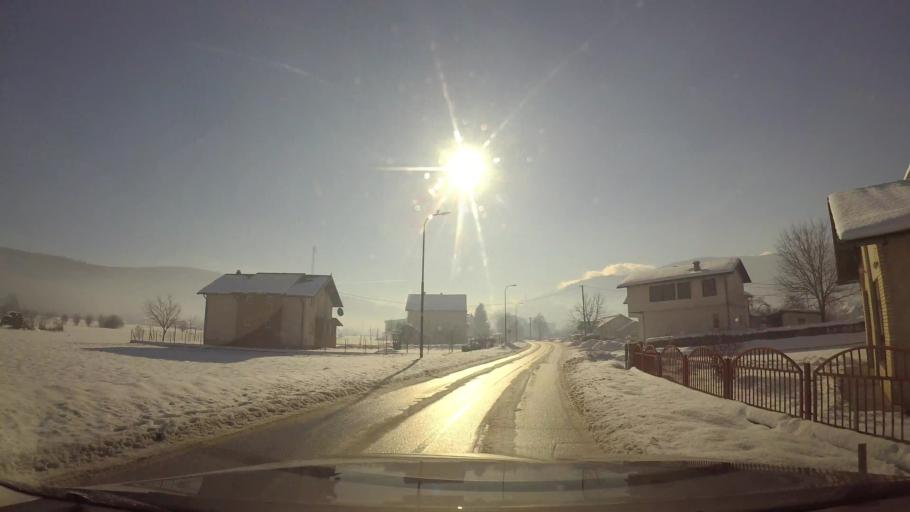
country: BA
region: Federation of Bosnia and Herzegovina
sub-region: Kanton Sarajevo
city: Sarajevo
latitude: 43.7959
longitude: 18.3521
